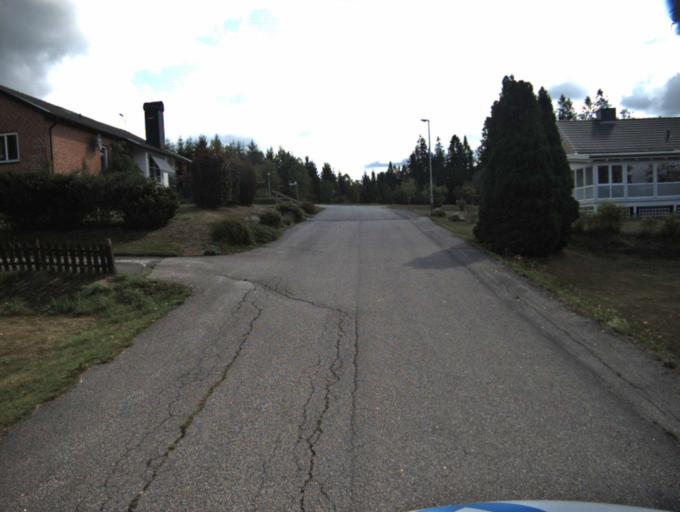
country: SE
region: Vaestra Goetaland
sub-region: Ulricehamns Kommun
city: Ulricehamn
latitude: 57.6993
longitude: 13.4994
